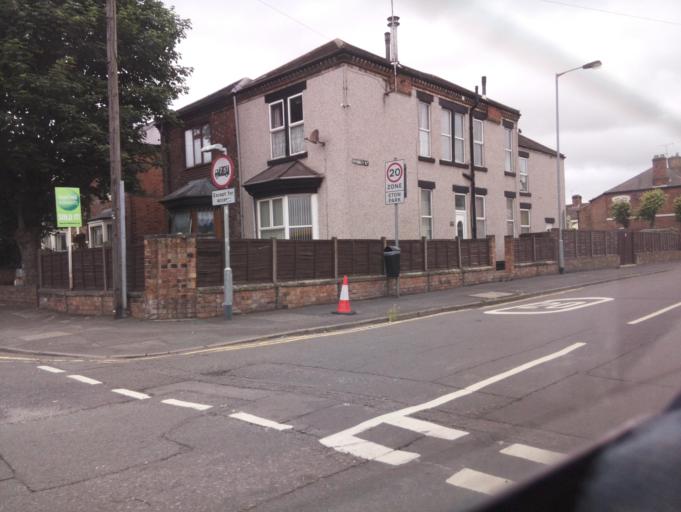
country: GB
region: England
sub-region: Staffordshire
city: Burton upon Trent
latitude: 52.8175
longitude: -1.6307
